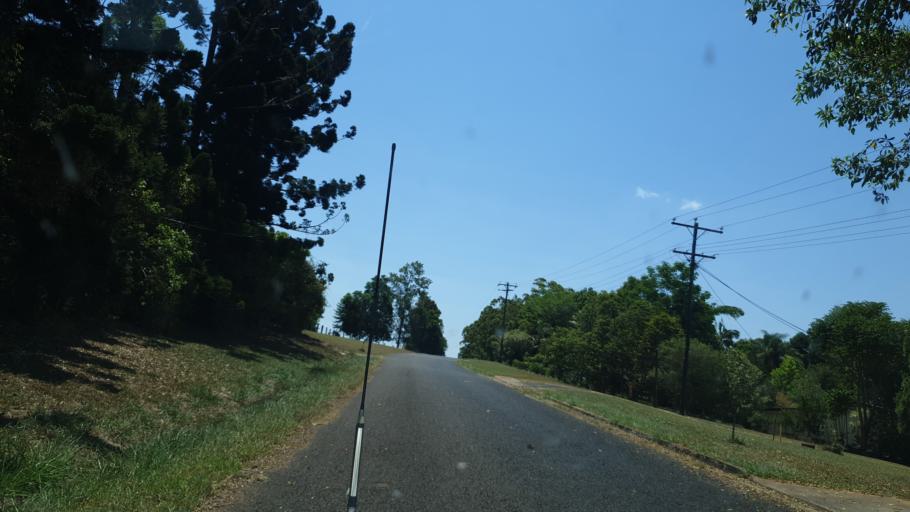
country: AU
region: Queensland
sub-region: Tablelands
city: Atherton
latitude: -17.3494
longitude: 145.6171
